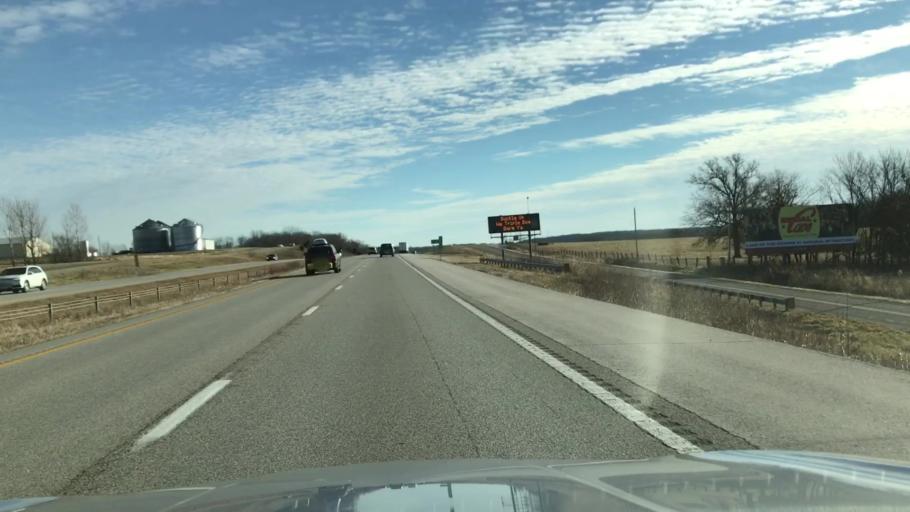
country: US
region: Missouri
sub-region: Saline County
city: Sweet Springs
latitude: 38.9707
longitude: -93.2592
